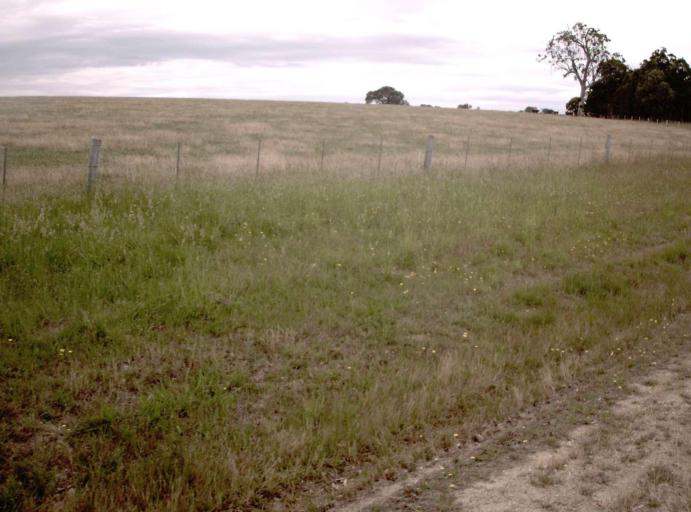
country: AU
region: Victoria
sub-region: East Gippsland
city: Bairnsdale
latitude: -37.7903
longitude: 147.3787
